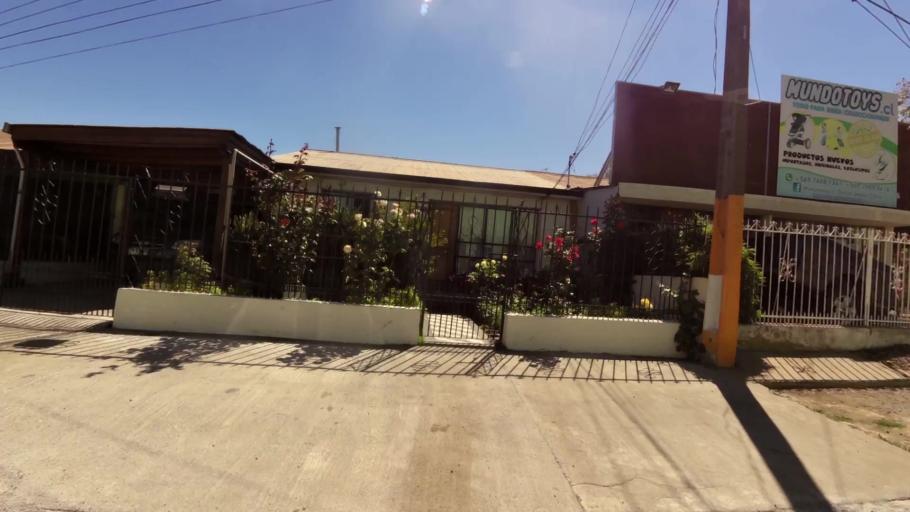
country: CL
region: O'Higgins
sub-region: Provincia de Cachapoal
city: Rancagua
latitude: -34.1770
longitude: -70.7149
